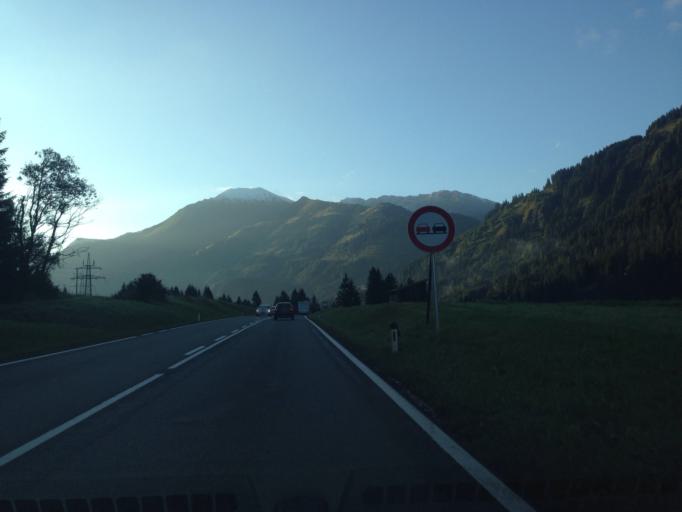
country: AT
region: Tyrol
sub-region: Politischer Bezirk Reutte
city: Bichlbach
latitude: 47.4315
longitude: 10.7748
